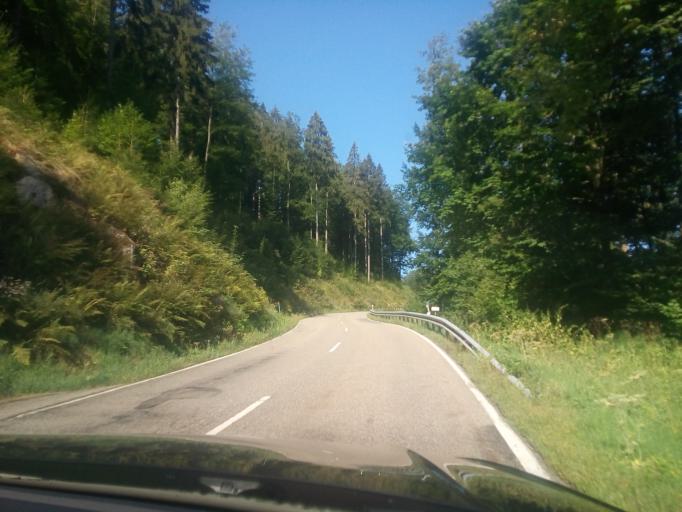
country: DE
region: Baden-Wuerttemberg
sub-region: Karlsruhe Region
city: Buhlertal
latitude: 48.6629
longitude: 8.2263
